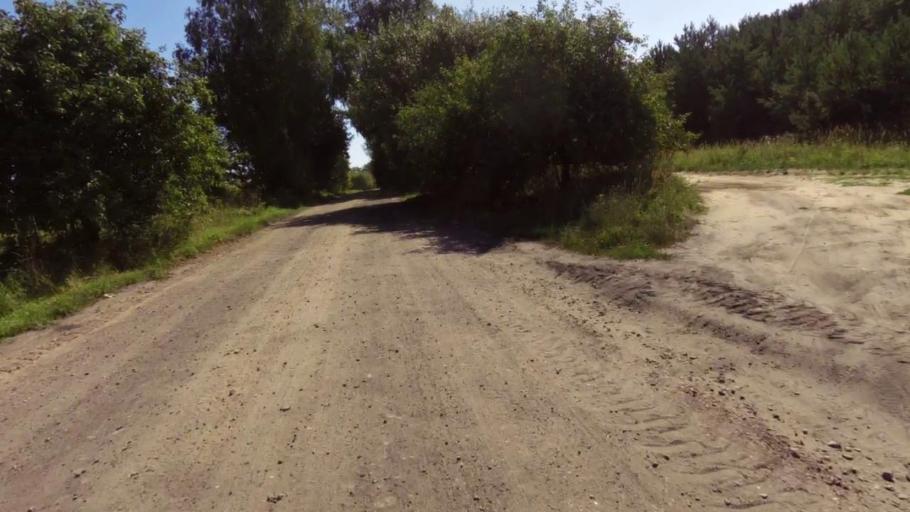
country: PL
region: West Pomeranian Voivodeship
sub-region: Powiat drawski
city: Zlocieniec
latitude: 53.5233
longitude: 16.0309
